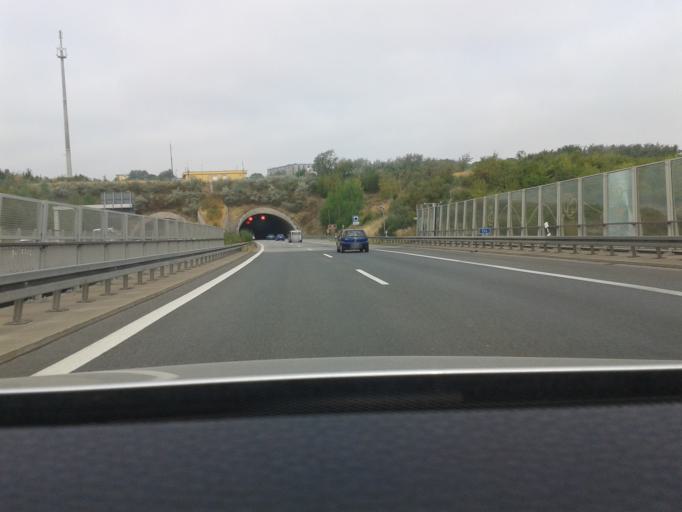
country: DE
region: Saxony
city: Bannewitz
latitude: 51.0123
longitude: 13.7195
